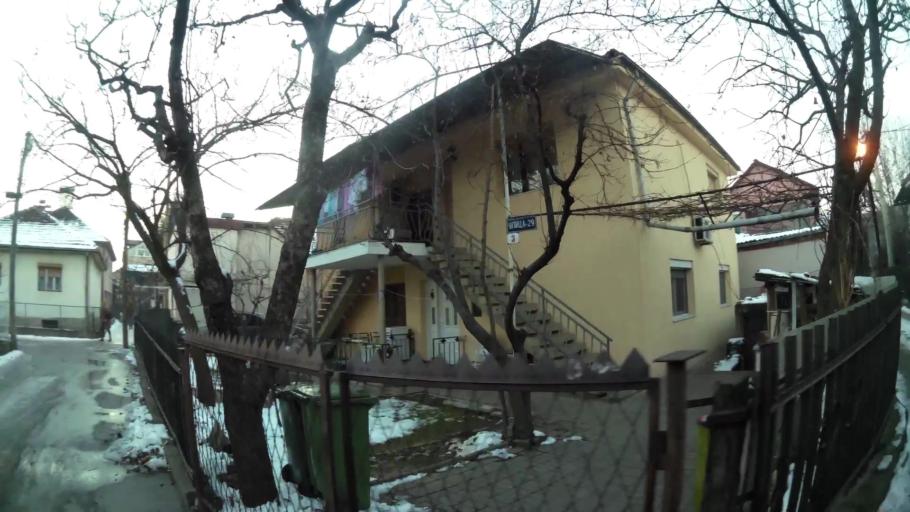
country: MK
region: Kisela Voda
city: Usje
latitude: 41.9814
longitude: 21.4858
